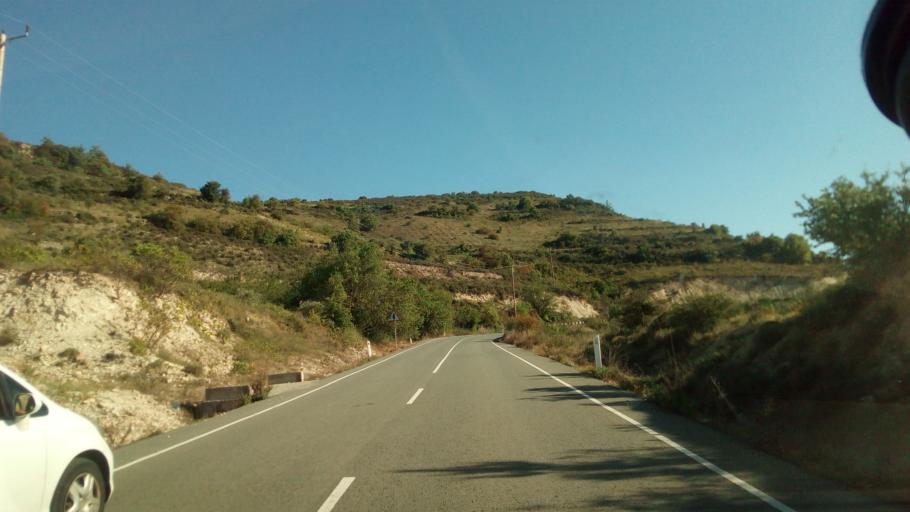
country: CY
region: Limassol
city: Pachna
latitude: 34.8593
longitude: 32.7607
